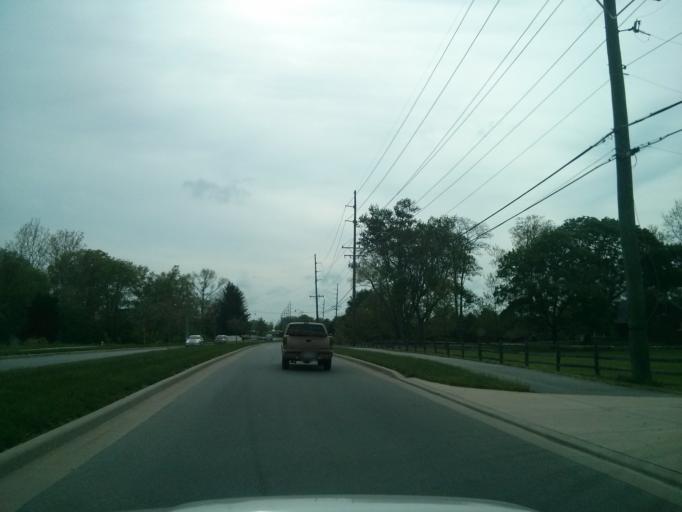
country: US
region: Indiana
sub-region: Hamilton County
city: Carmel
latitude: 39.9777
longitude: -86.1764
